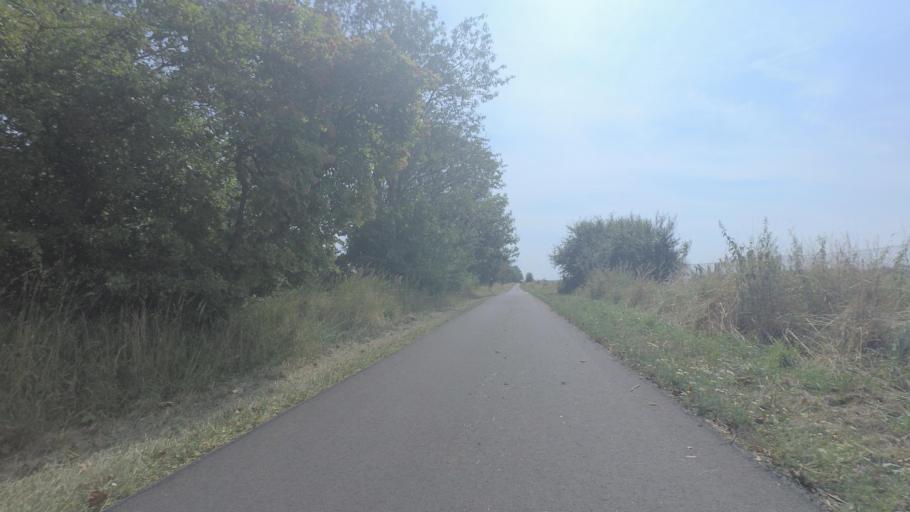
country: DE
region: Mecklenburg-Vorpommern
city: Garz
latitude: 54.2741
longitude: 13.3456
